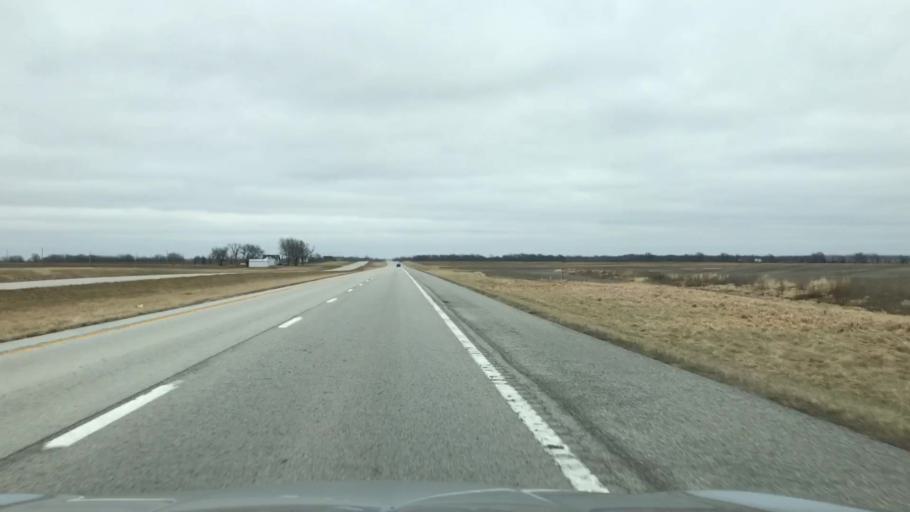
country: US
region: Missouri
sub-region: Livingston County
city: Chillicothe
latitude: 39.7762
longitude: -93.4694
